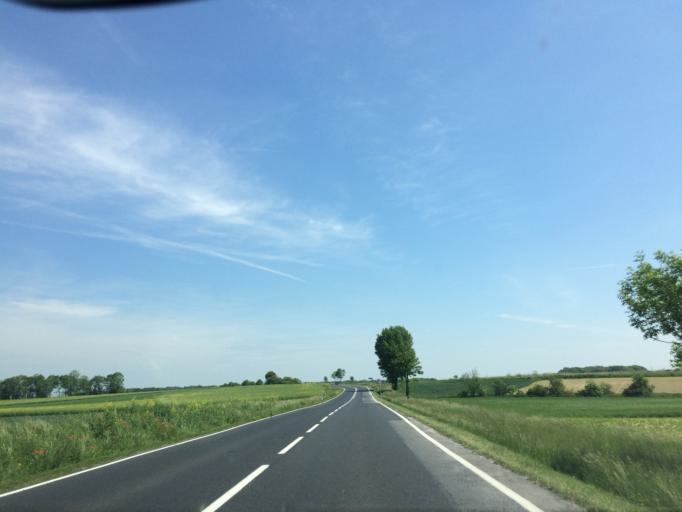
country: PL
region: Lower Silesian Voivodeship
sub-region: Powiat wroclawski
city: Gniechowice
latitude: 50.9703
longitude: 16.8054
